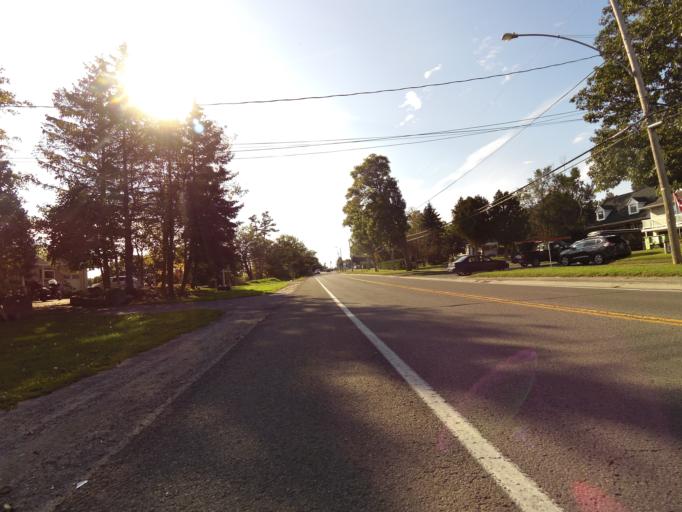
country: CA
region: Ontario
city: Kingston
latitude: 44.2195
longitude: -76.6399
